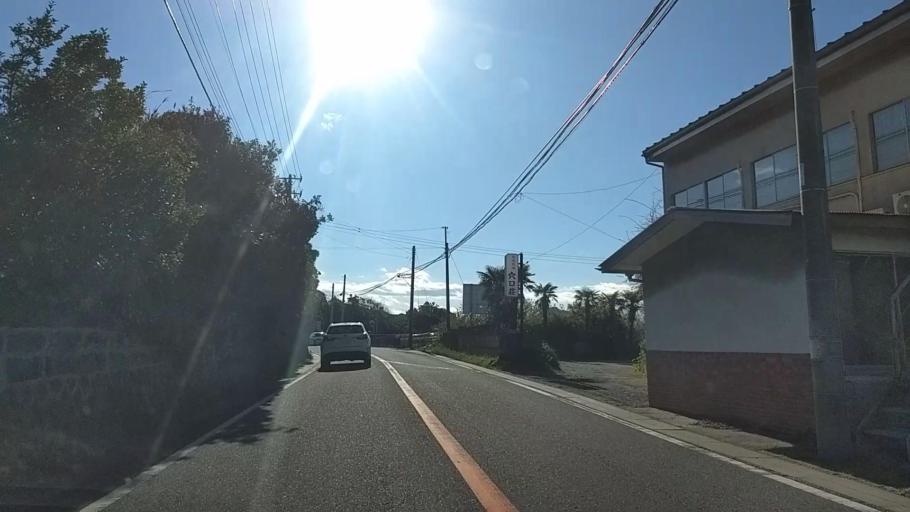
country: JP
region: Chiba
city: Futtsu
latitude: 35.1456
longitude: 139.8334
